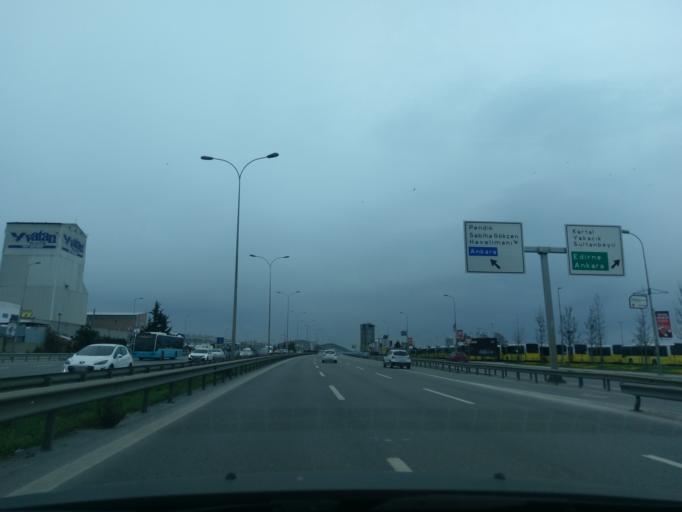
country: TR
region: Istanbul
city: Maltepe
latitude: 40.9088
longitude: 29.2054
